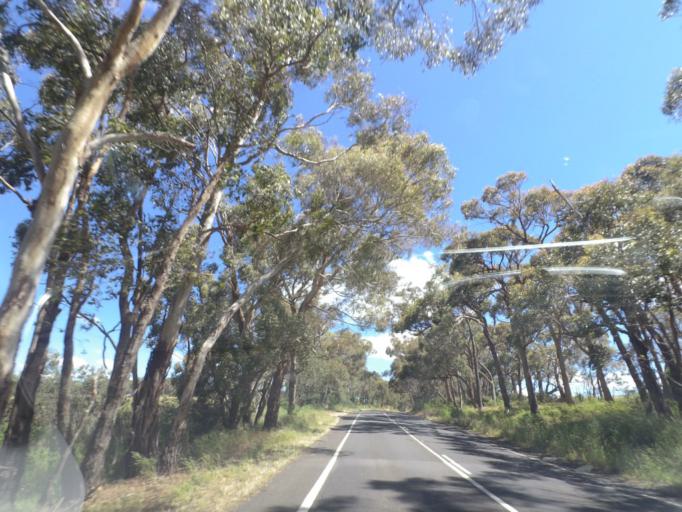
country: AU
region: Victoria
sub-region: Mount Alexander
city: Castlemaine
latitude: -37.3074
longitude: 144.4137
